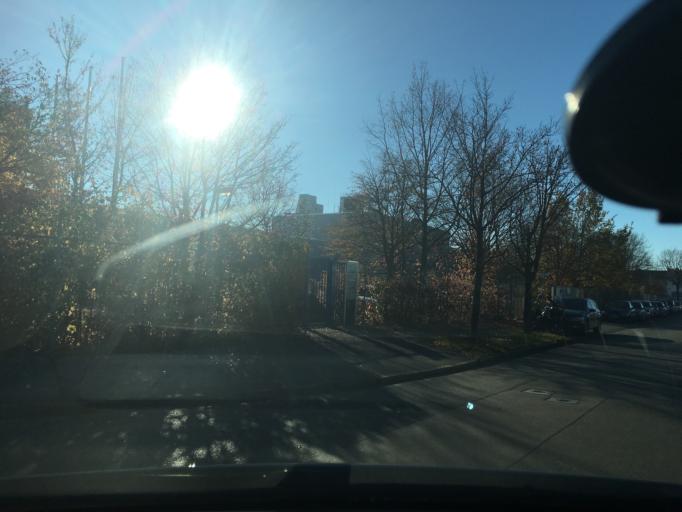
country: DE
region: Bavaria
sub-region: Upper Bavaria
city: Garching bei Munchen
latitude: 48.2475
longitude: 11.6251
